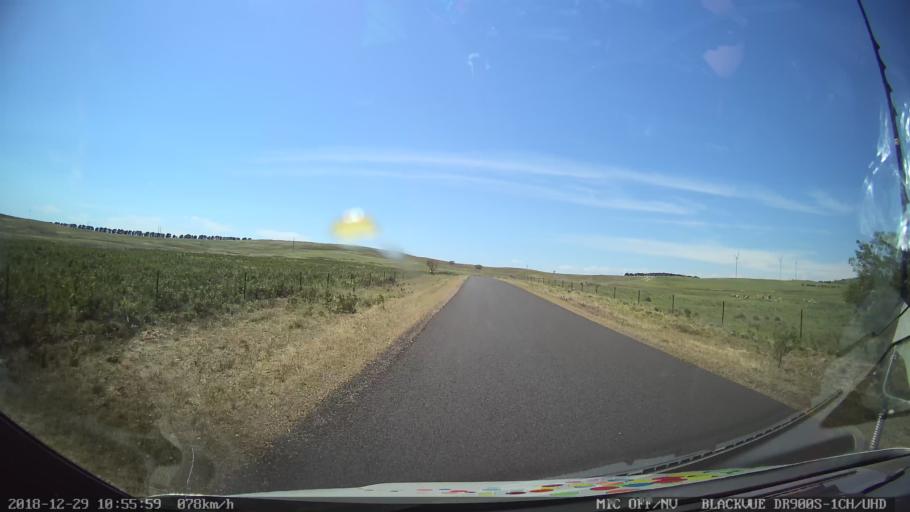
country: AU
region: New South Wales
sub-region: Palerang
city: Bungendore
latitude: -35.1298
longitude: 149.5352
